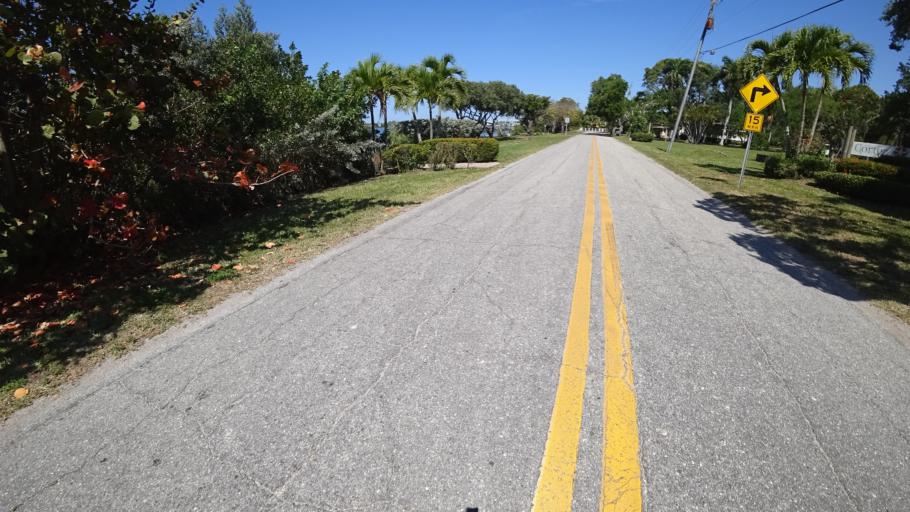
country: US
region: Florida
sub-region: Manatee County
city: Cortez
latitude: 27.4716
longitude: -82.6904
